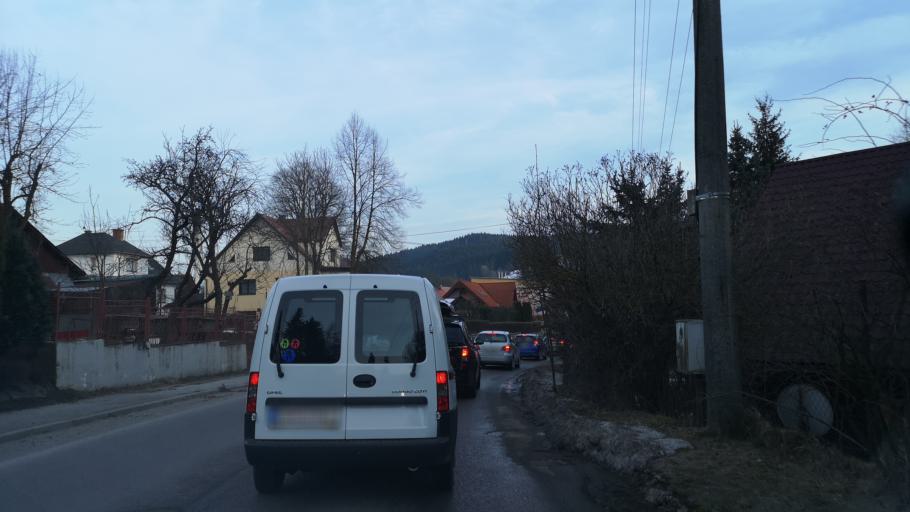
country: SK
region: Zilinsky
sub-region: Okres Dolny Kubin
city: Dolny Kubin
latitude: 49.2133
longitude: 19.2709
